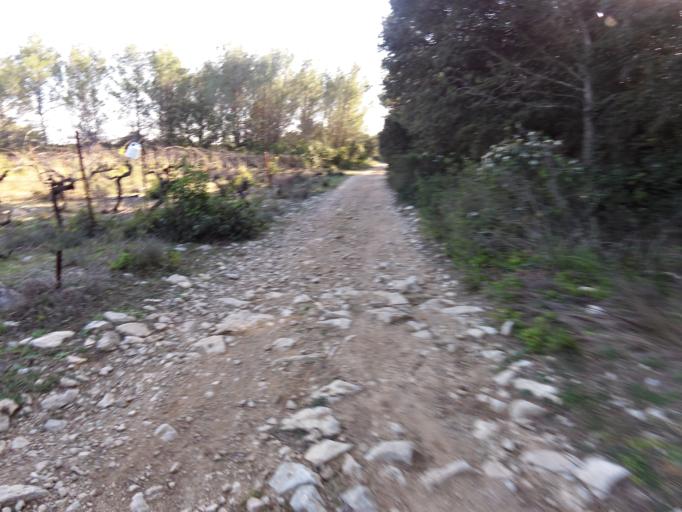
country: FR
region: Languedoc-Roussillon
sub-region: Departement du Gard
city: Congenies
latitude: 43.7582
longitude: 4.1707
